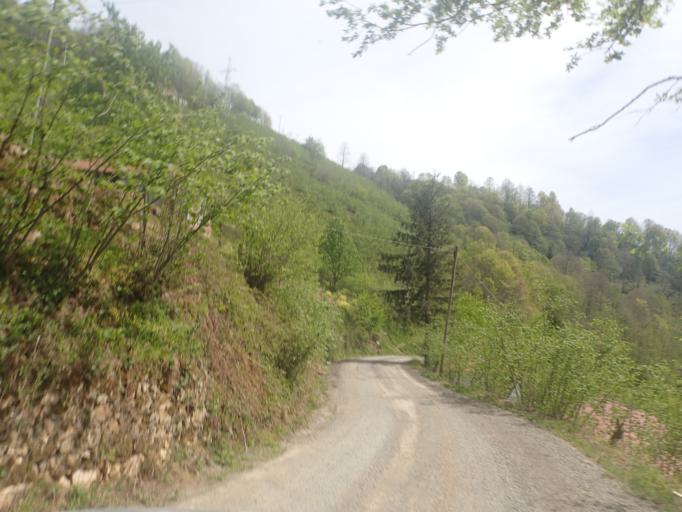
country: TR
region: Ordu
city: Kabaduz
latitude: 40.8010
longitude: 37.9080
